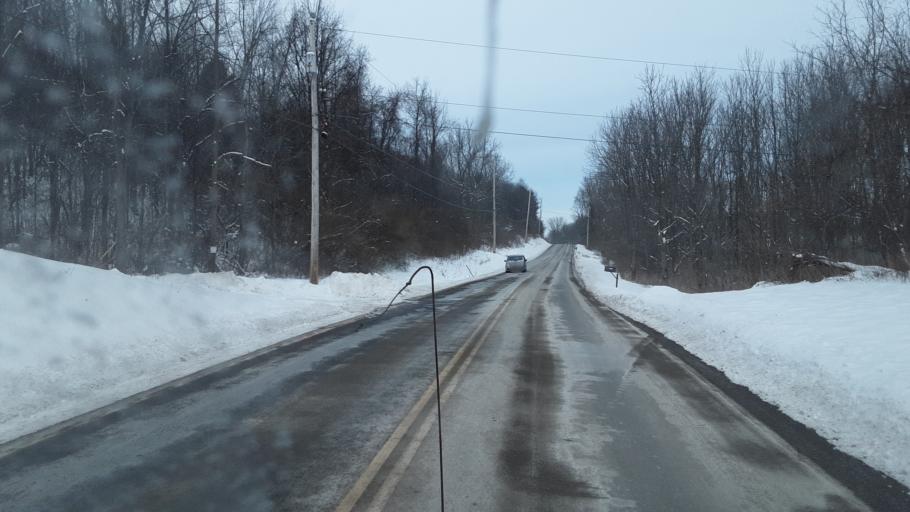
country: US
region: New York
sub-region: Wayne County
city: Newark
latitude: 43.0634
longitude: -77.0542
